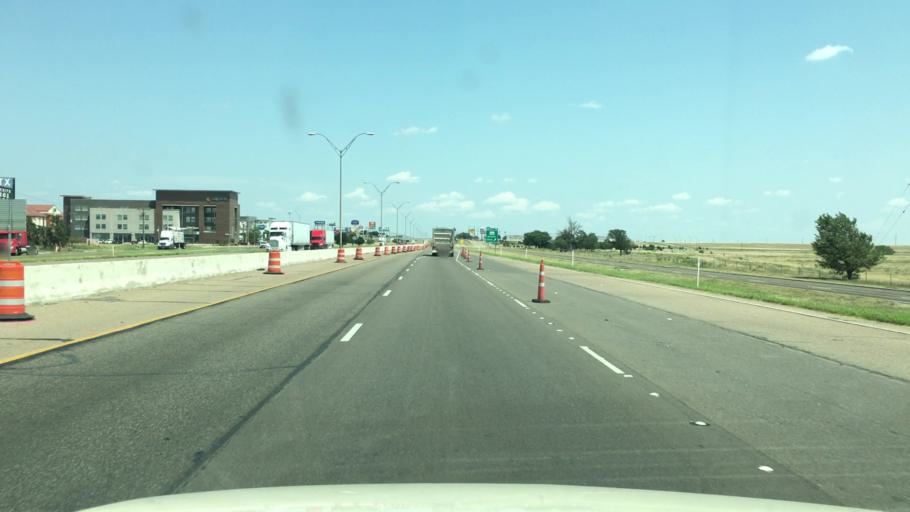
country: US
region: Texas
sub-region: Potter County
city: Amarillo
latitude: 35.1927
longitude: -101.7350
